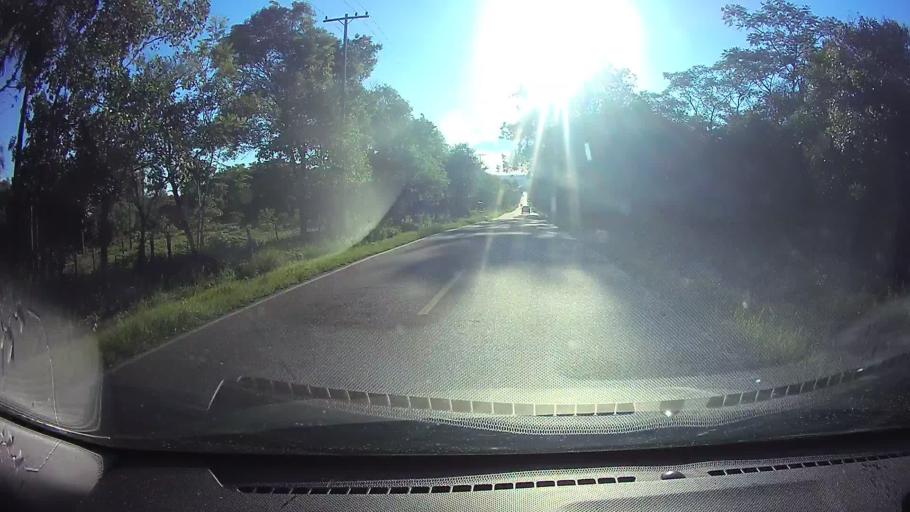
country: PY
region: Cordillera
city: Emboscada
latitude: -25.2019
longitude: -57.3289
